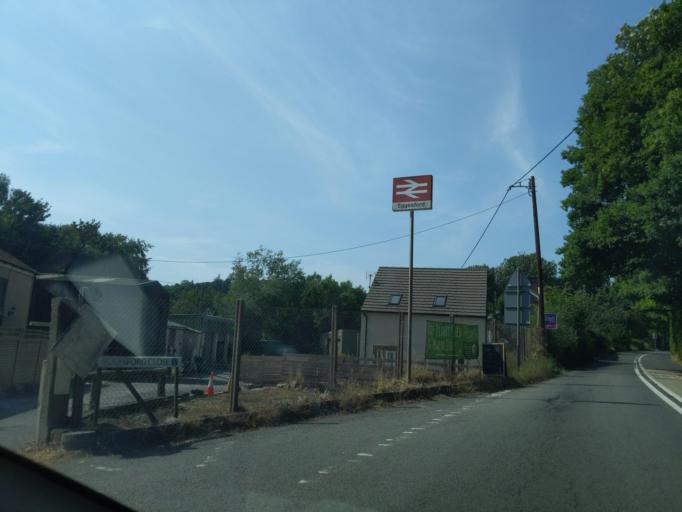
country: GB
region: England
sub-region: Devon
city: Winkleigh
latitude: 50.8879
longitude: -3.8748
